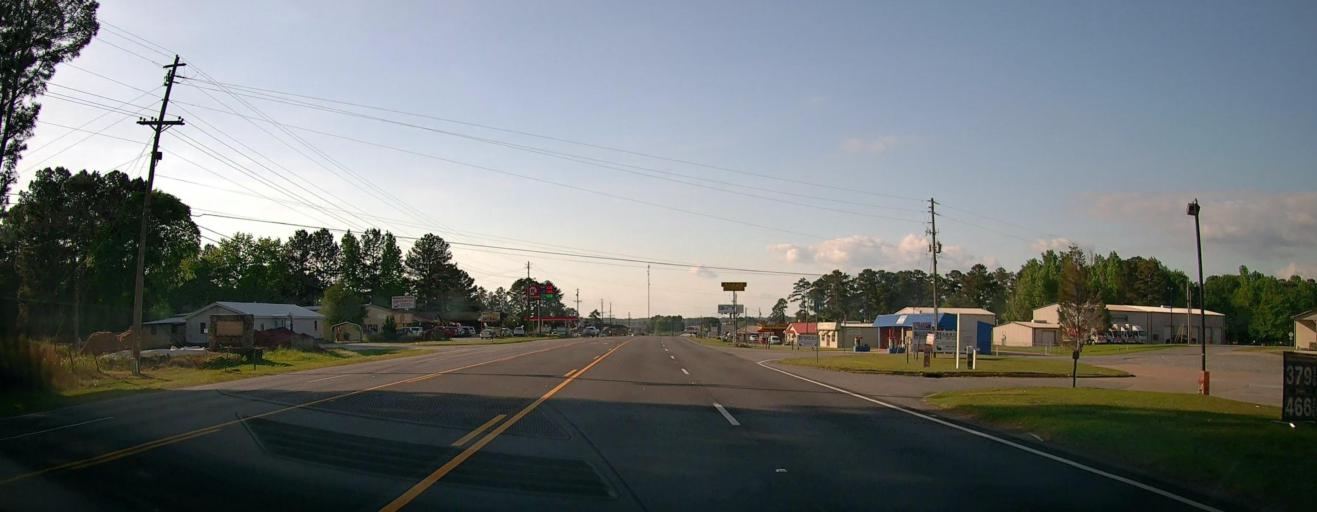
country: US
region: Georgia
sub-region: Baldwin County
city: Milledgeville
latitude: 33.1822
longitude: -83.2893
